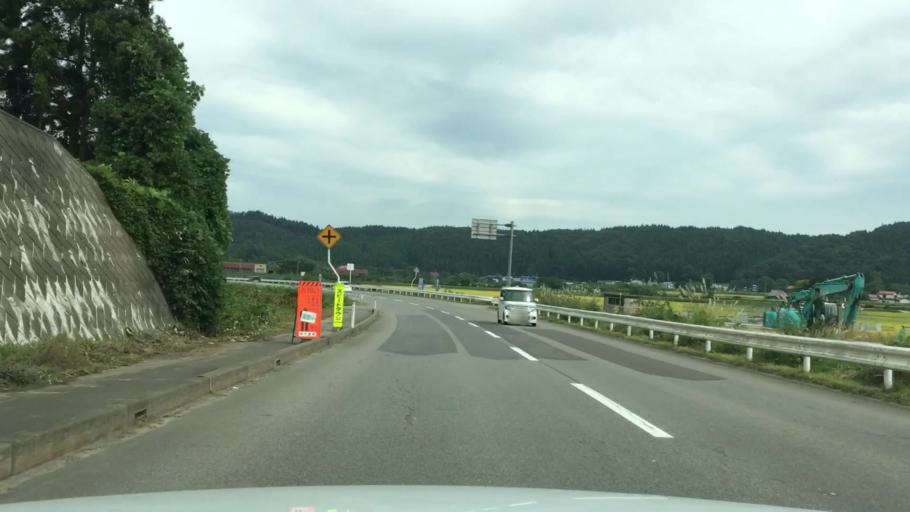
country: JP
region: Aomori
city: Shimokizukuri
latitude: 40.7526
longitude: 140.2300
